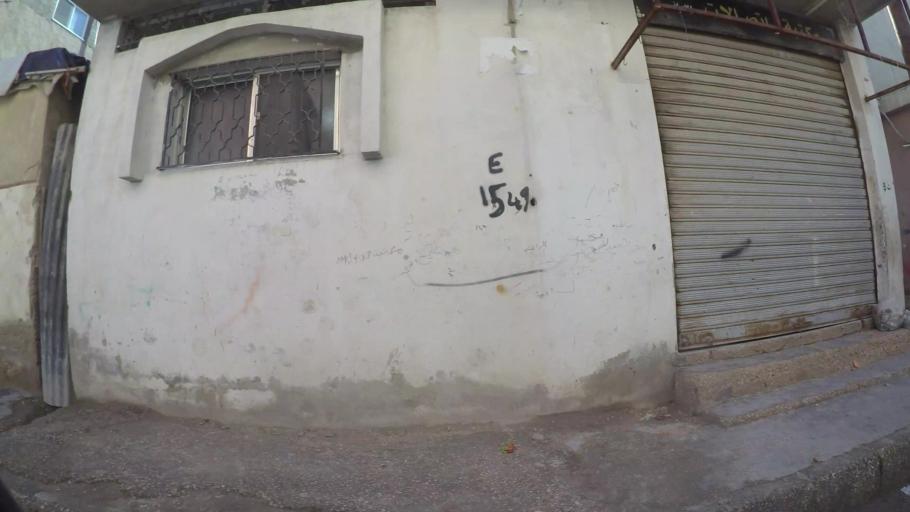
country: JO
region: Amman
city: Al Jubayhah
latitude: 32.0654
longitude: 35.8437
